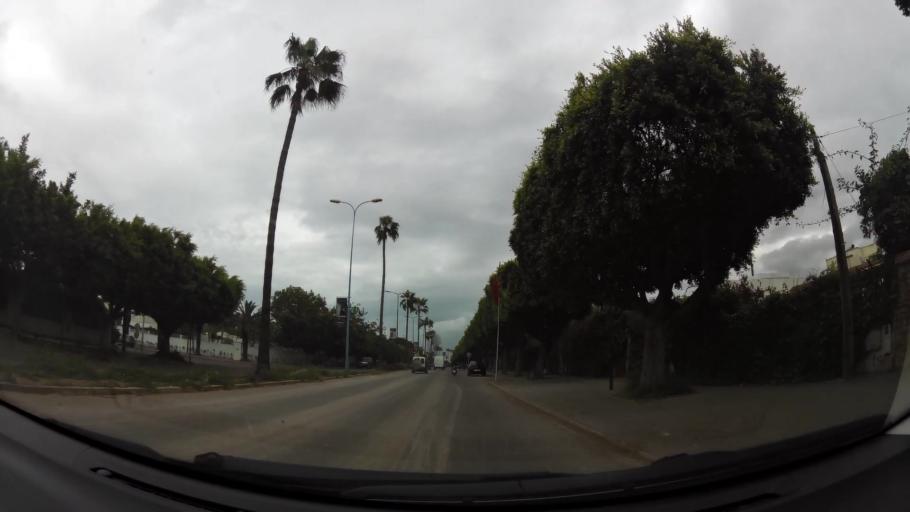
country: MA
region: Grand Casablanca
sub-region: Casablanca
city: Casablanca
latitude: 33.5786
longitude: -7.6702
